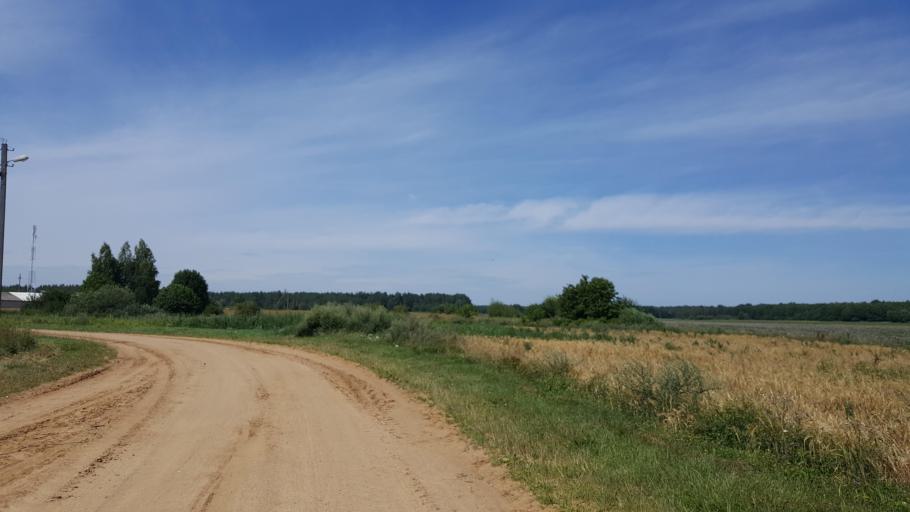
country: BY
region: Brest
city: Pruzhany
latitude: 52.5653
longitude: 24.2259
